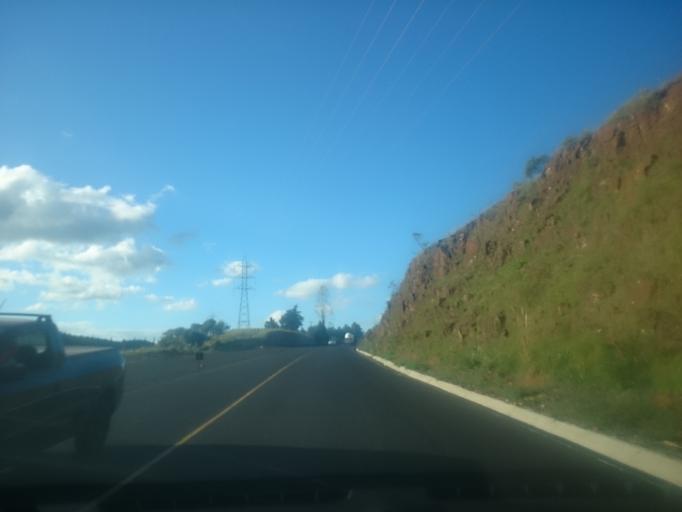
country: BR
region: Santa Catarina
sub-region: Sao Joaquim
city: Sao Joaquim
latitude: -28.0572
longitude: -50.0738
